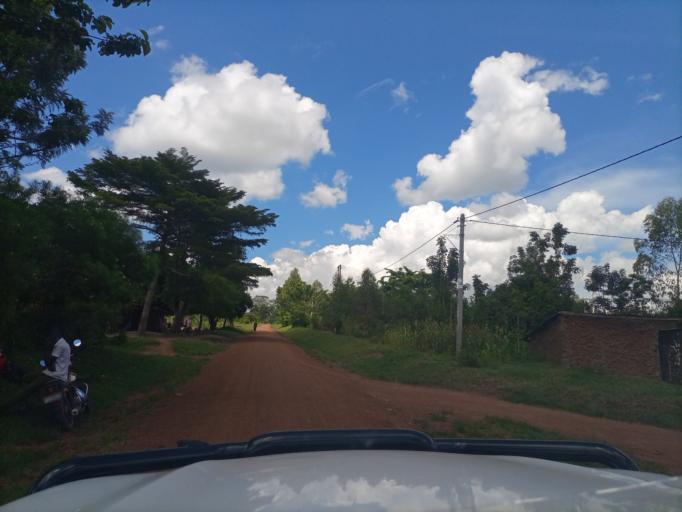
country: UG
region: Eastern Region
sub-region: Tororo District
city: Tororo
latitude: 0.7039
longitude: 34.0135
